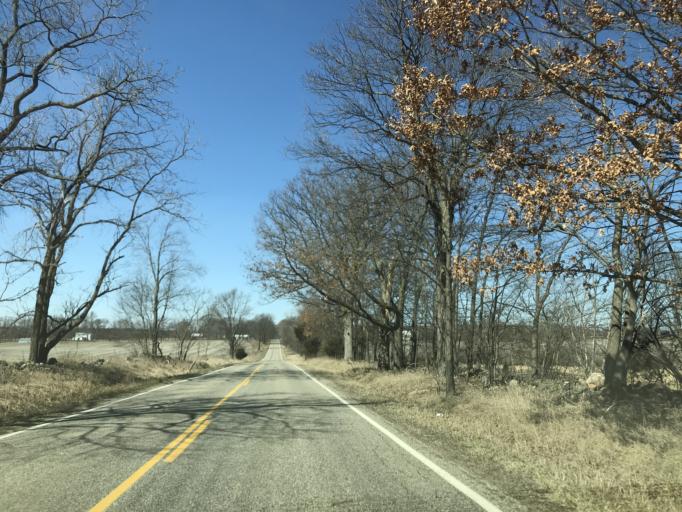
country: US
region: Michigan
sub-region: Hillsdale County
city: Litchfield
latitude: 41.9855
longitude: -84.7315
